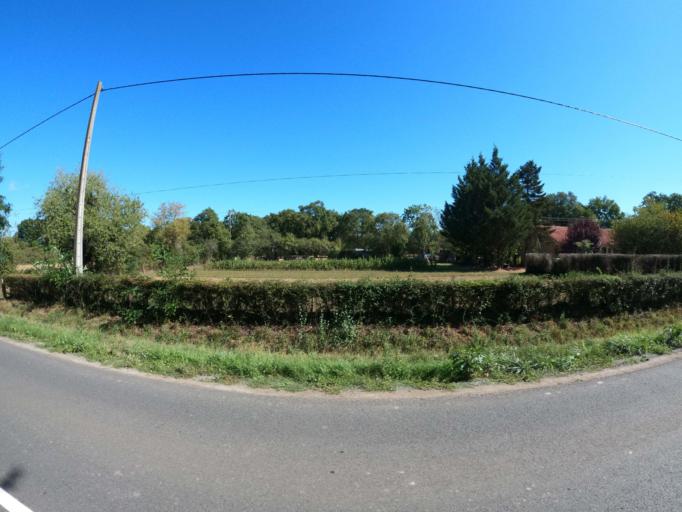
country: FR
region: Poitou-Charentes
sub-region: Departement de la Vienne
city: Lathus-Saint-Remy
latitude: 46.3656
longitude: 0.9386
